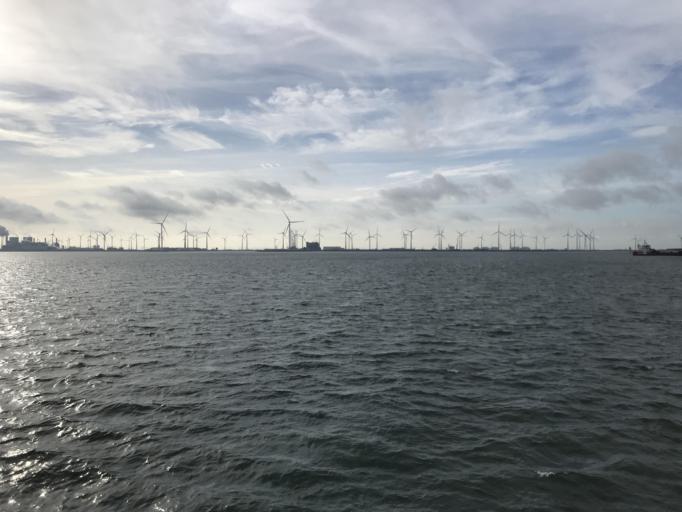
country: NL
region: Groningen
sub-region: Gemeente Appingedam
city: Appingedam
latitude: 53.4856
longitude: 6.8372
